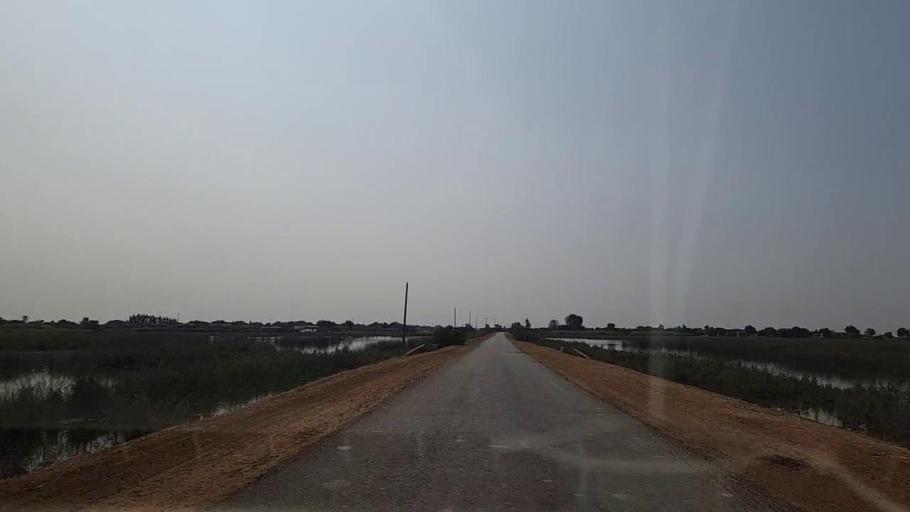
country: PK
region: Sindh
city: Chuhar Jamali
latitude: 24.3090
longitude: 67.9382
